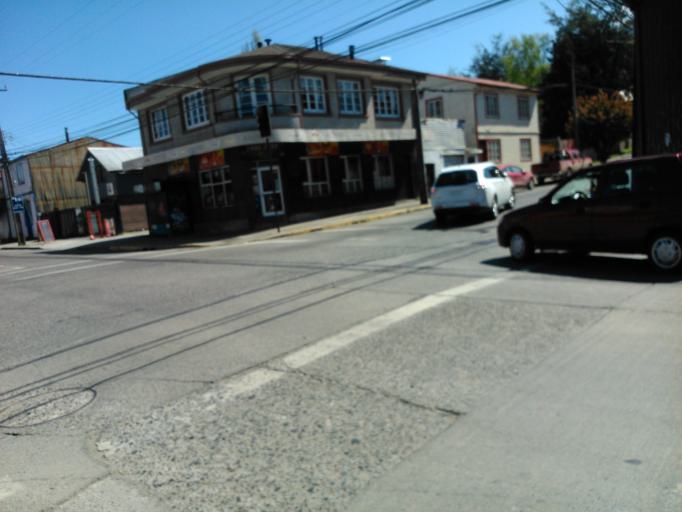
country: CL
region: Los Rios
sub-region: Provincia de Valdivia
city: Valdivia
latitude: -39.8191
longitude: -73.2475
